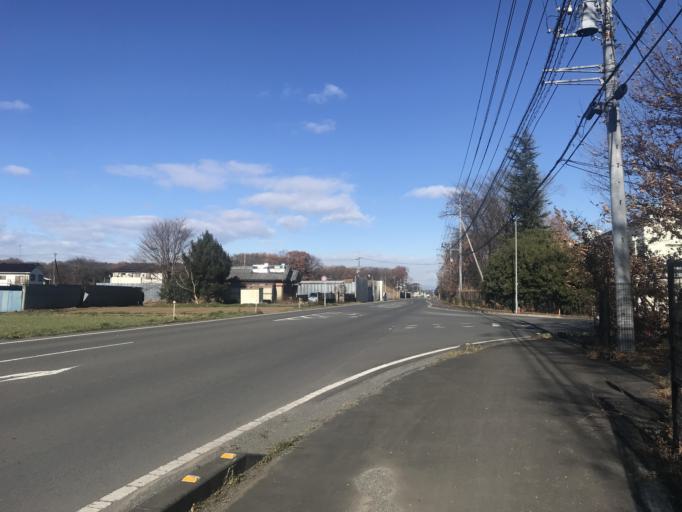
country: JP
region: Ibaraki
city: Yuki
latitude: 36.3448
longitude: 139.8787
